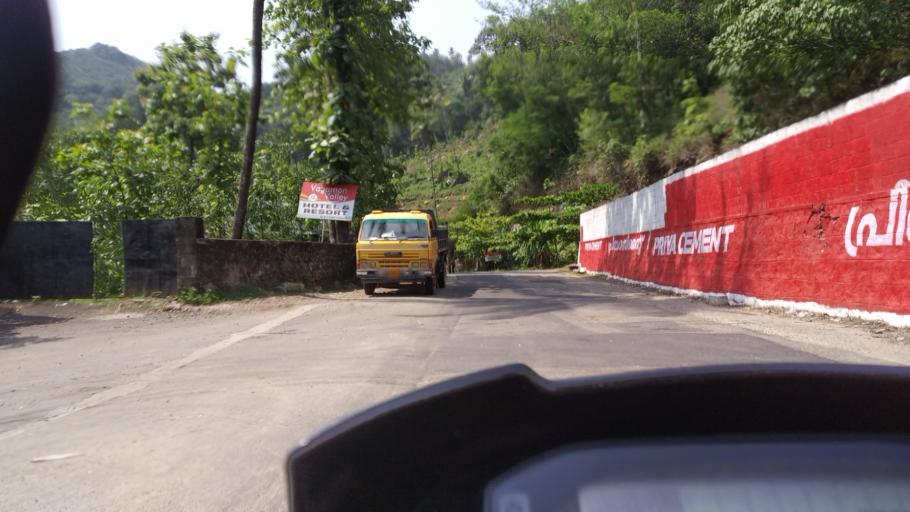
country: IN
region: Kerala
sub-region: Kottayam
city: Erattupetta
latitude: 9.6879
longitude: 76.8272
